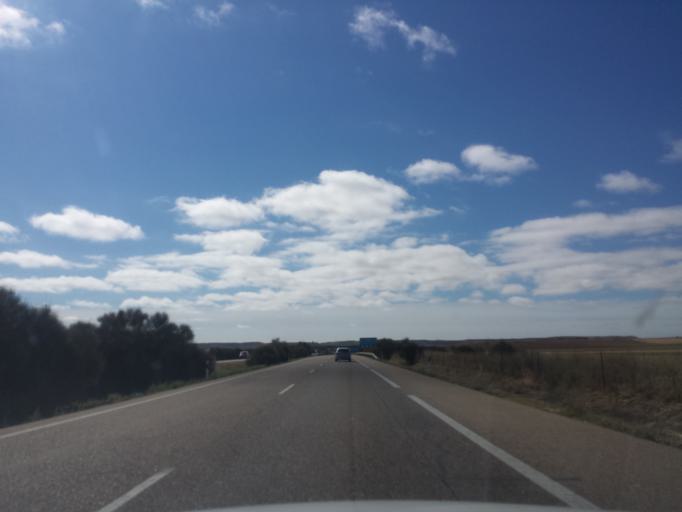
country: ES
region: Castille and Leon
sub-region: Provincia de Valladolid
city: Villardefrades
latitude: 41.7400
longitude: -5.2702
